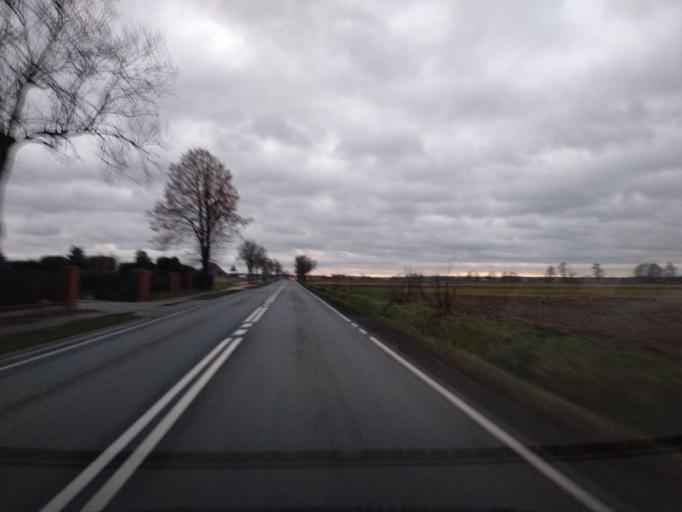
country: PL
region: Greater Poland Voivodeship
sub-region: Powiat koninski
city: Rychwal
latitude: 52.1150
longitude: 18.1676
